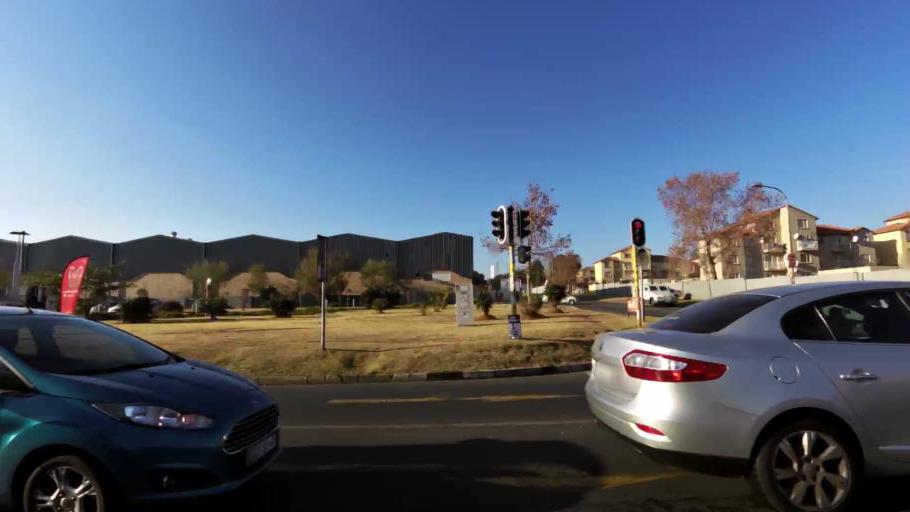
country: ZA
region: Gauteng
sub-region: City of Johannesburg Metropolitan Municipality
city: Johannesburg
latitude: -26.2389
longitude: 28.0081
